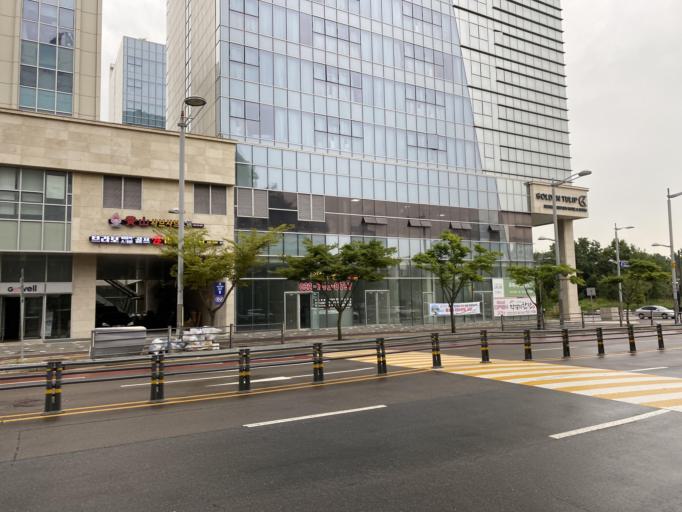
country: KR
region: Incheon
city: Incheon
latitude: 37.4923
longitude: 126.4920
